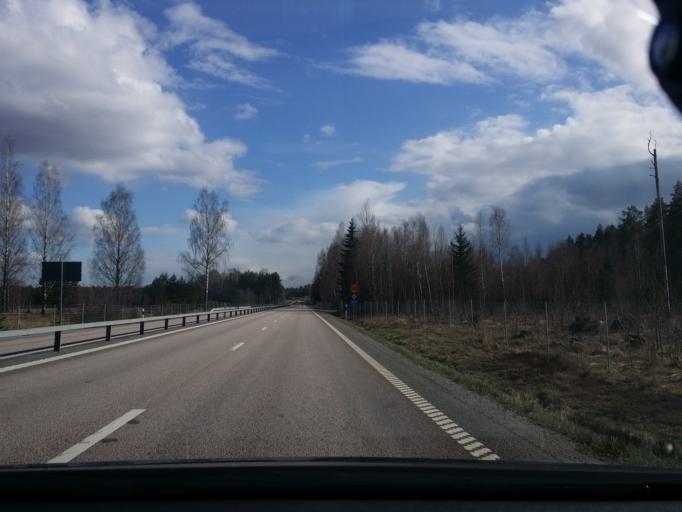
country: SE
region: Vaestmanland
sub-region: Sala Kommun
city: Sala
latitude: 59.8267
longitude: 16.5337
